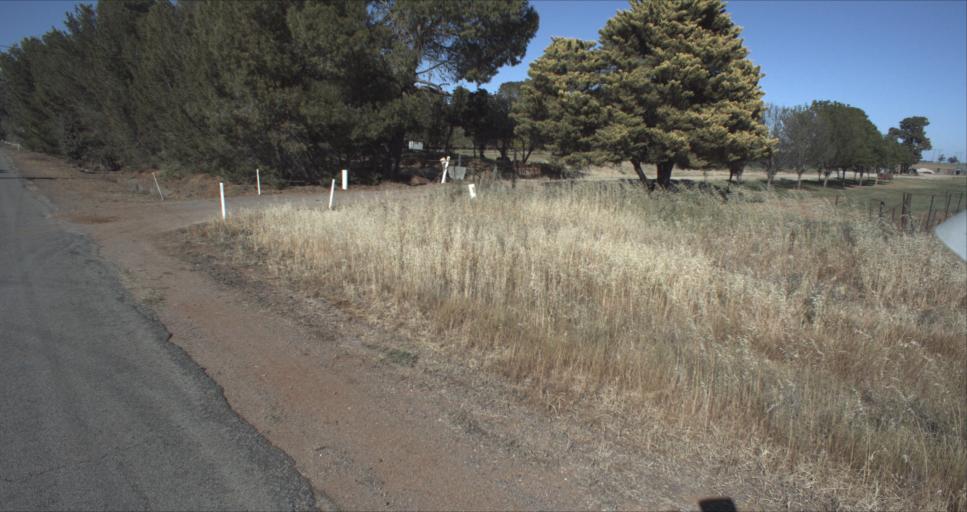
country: AU
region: New South Wales
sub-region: Leeton
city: Leeton
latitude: -34.5717
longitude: 146.3105
